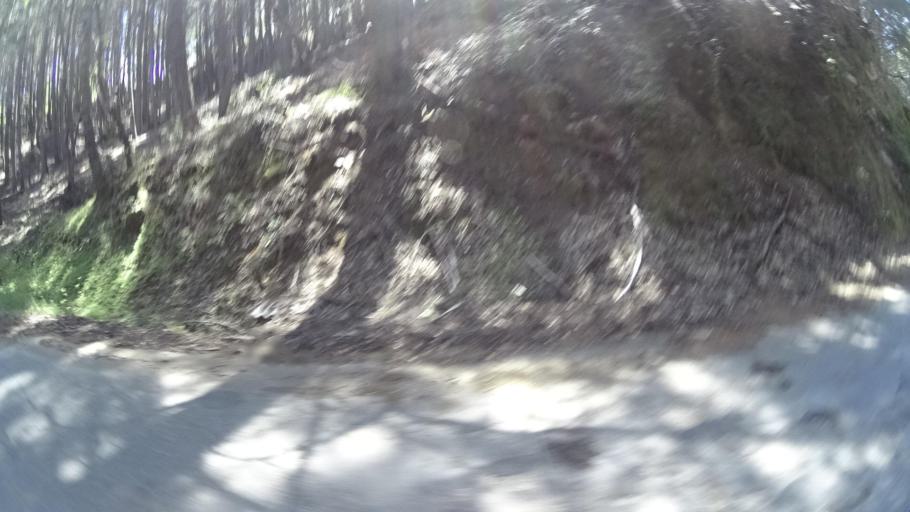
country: US
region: California
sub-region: Humboldt County
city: Rio Dell
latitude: 40.2645
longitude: -124.0924
